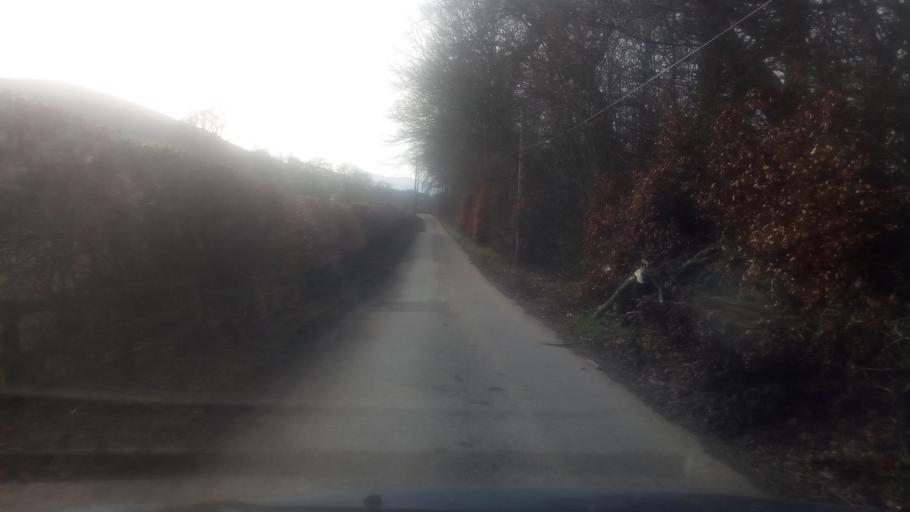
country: GB
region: Scotland
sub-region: The Scottish Borders
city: Jedburgh
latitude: 55.4132
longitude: -2.6475
